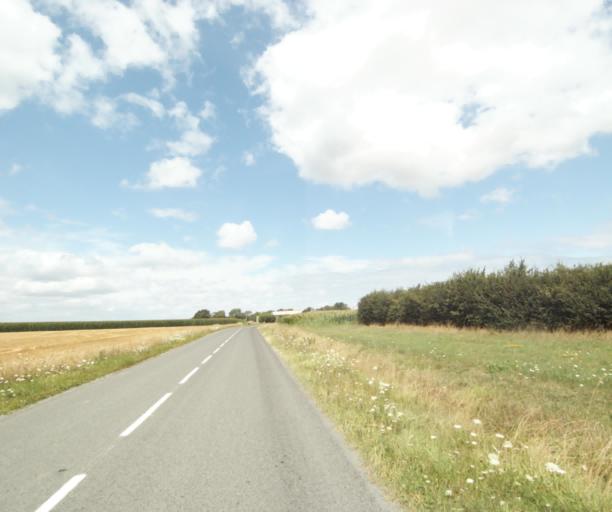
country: FR
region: Pays de la Loire
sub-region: Departement de la Sarthe
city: Sable-sur-Sarthe
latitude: 47.8510
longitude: -0.3309
